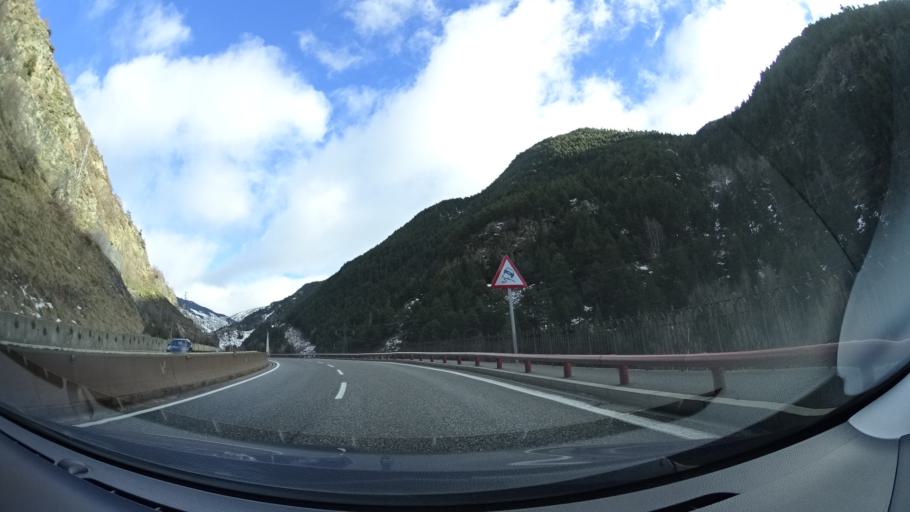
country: AD
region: Canillo
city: Canillo
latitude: 42.5714
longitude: 1.6104
